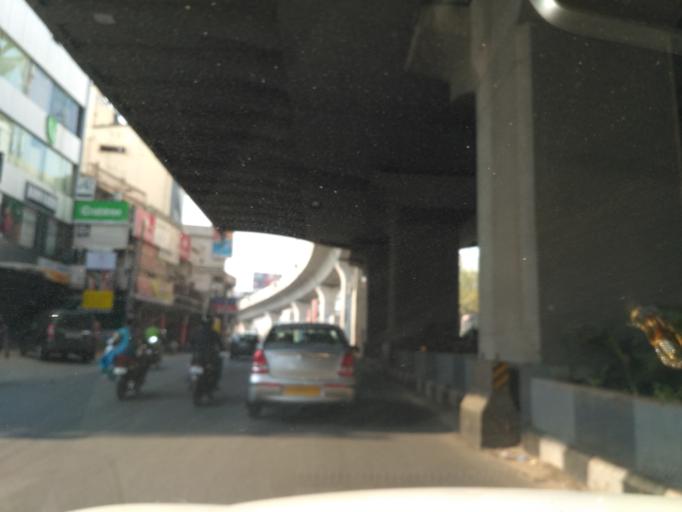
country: IN
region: Telangana
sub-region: Rangareddi
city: Kukatpalli
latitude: 17.4431
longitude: 78.3875
